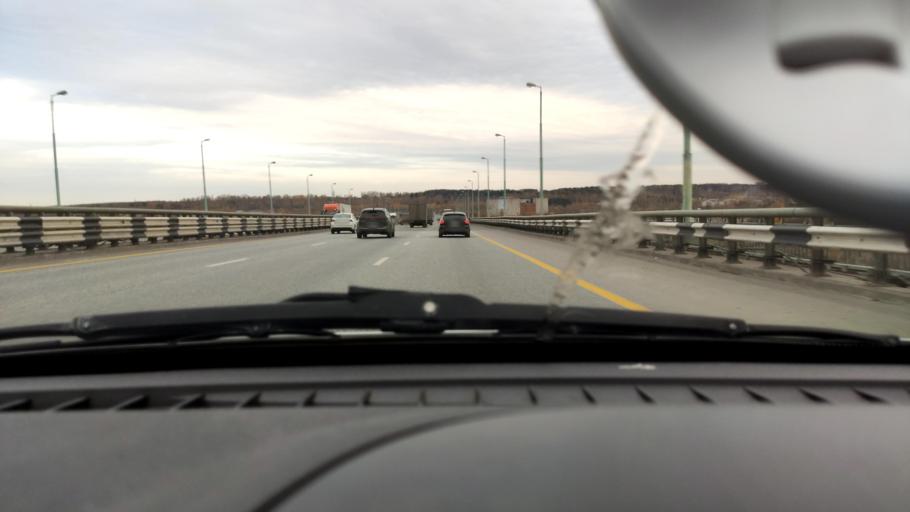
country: RU
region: Perm
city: Kondratovo
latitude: 58.0238
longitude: 56.0542
